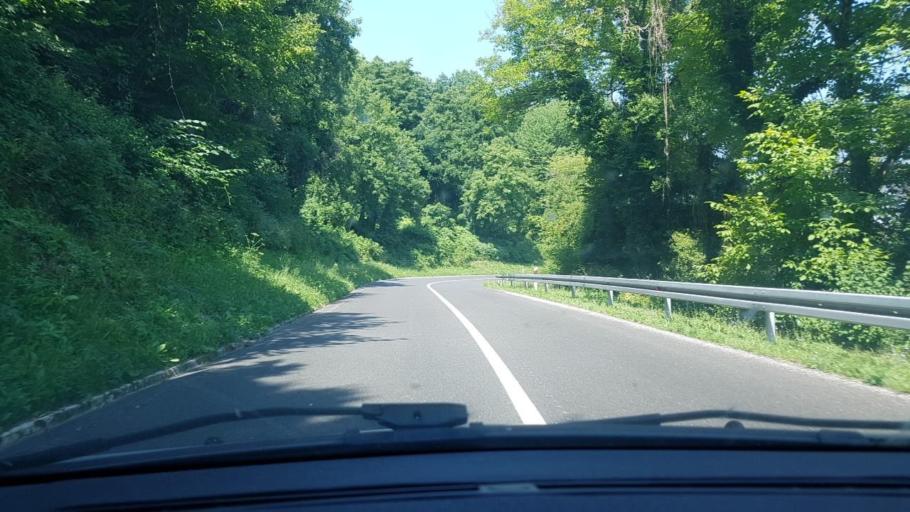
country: HR
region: Karlovacka
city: Vojnic
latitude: 45.2454
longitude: 15.7262
